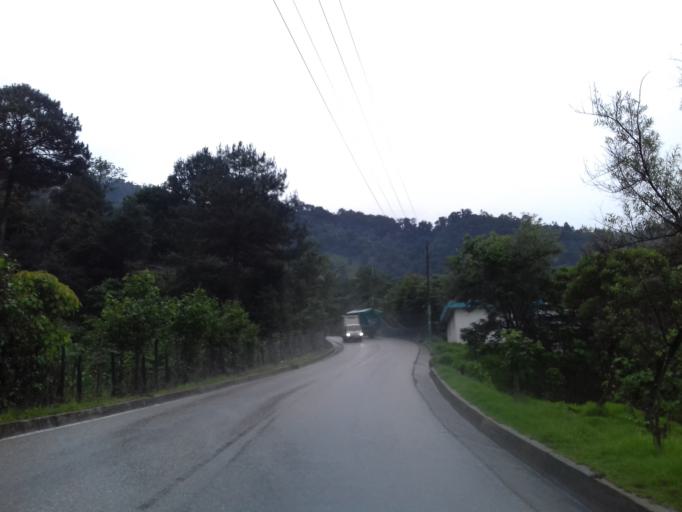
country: GT
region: Quiche
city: Nebaj
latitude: 15.3831
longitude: -91.1111
